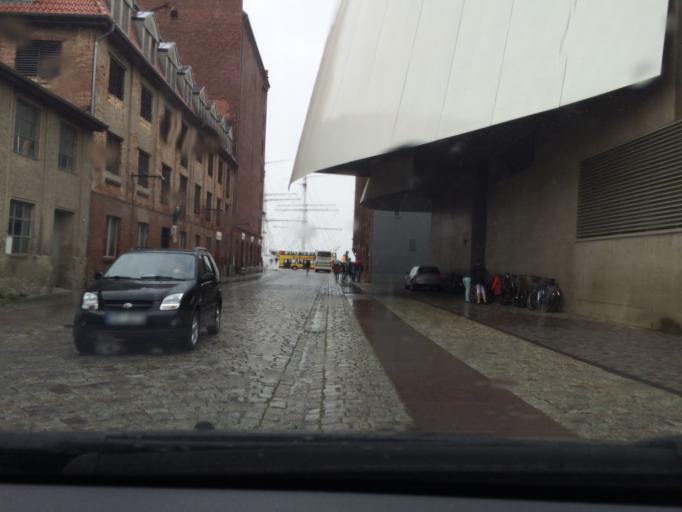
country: DE
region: Mecklenburg-Vorpommern
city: Stralsund
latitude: 54.3159
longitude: 13.0961
